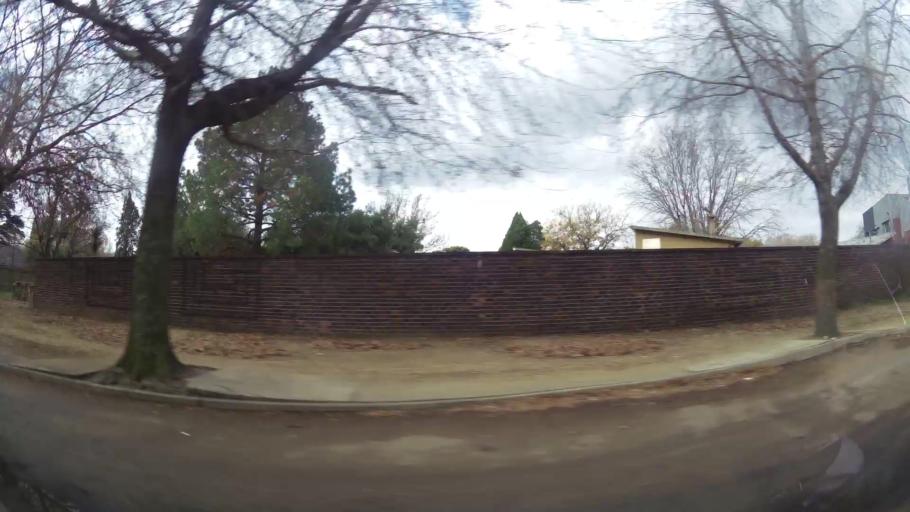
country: ZA
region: Orange Free State
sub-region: Fezile Dabi District Municipality
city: Sasolburg
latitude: -26.8129
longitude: 27.8292
